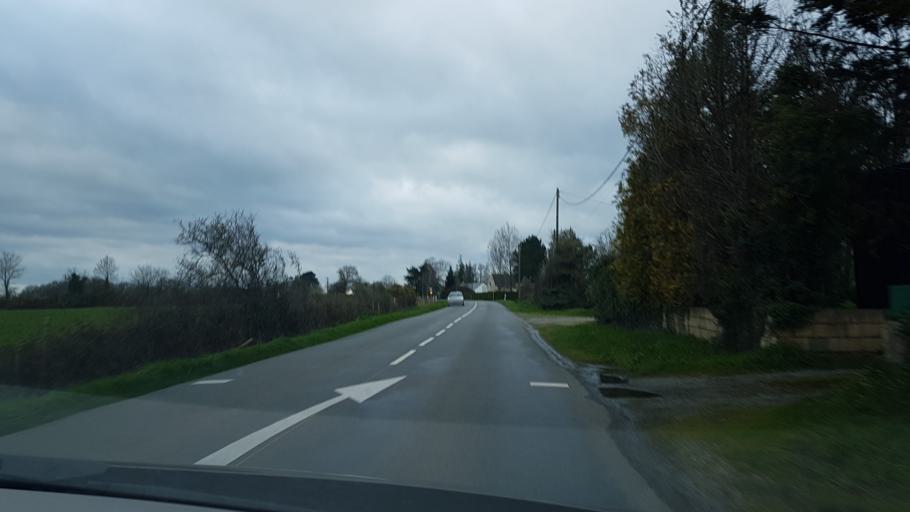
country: FR
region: Pays de la Loire
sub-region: Departement de la Loire-Atlantique
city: La Grigonnais
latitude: 47.5184
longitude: -1.6647
